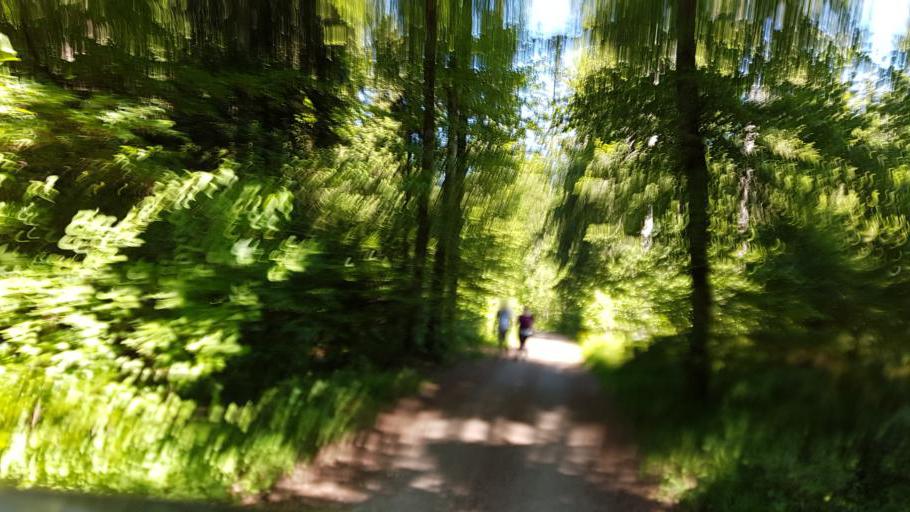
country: CH
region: Bern
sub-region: Thun District
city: Thun
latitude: 46.7220
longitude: 7.6055
